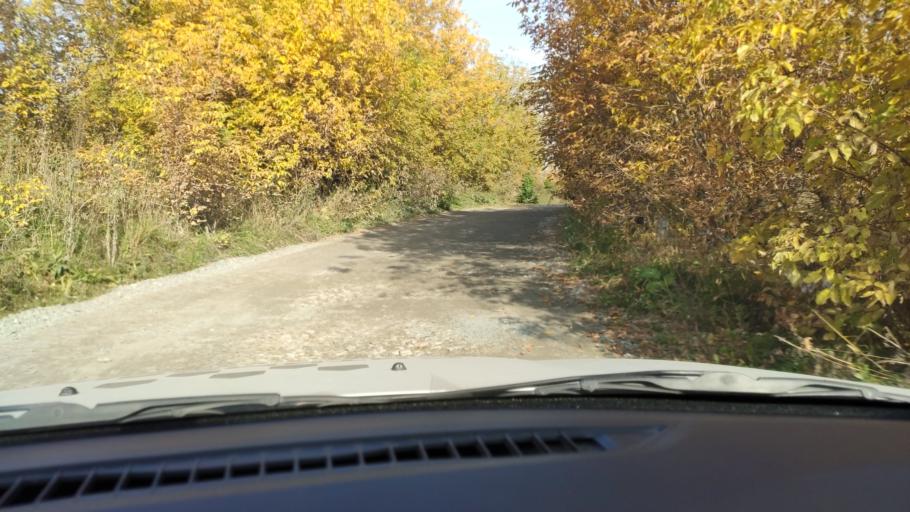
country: RU
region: Perm
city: Sylva
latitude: 58.0435
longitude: 56.7464
